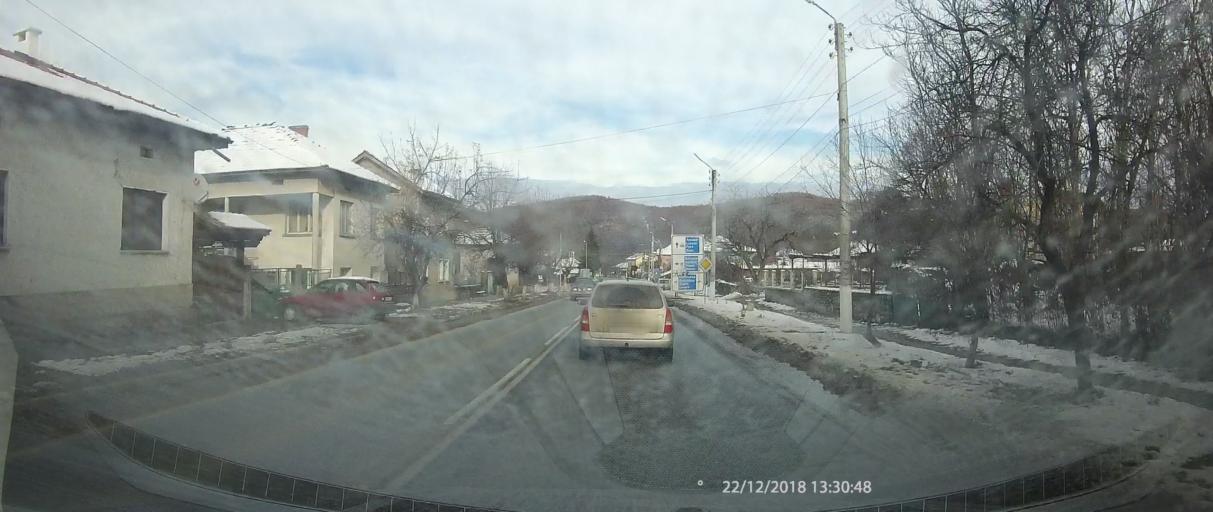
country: BG
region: Lovech
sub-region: Obshtina Yablanitsa
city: Yablanitsa
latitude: 43.0911
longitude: 24.1495
